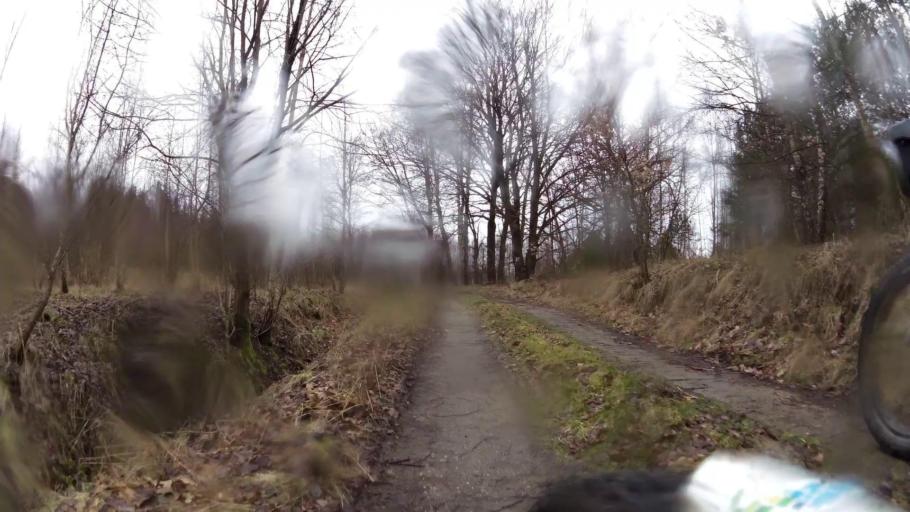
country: PL
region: Pomeranian Voivodeship
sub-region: Powiat bytowski
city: Miastko
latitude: 54.0404
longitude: 17.0411
